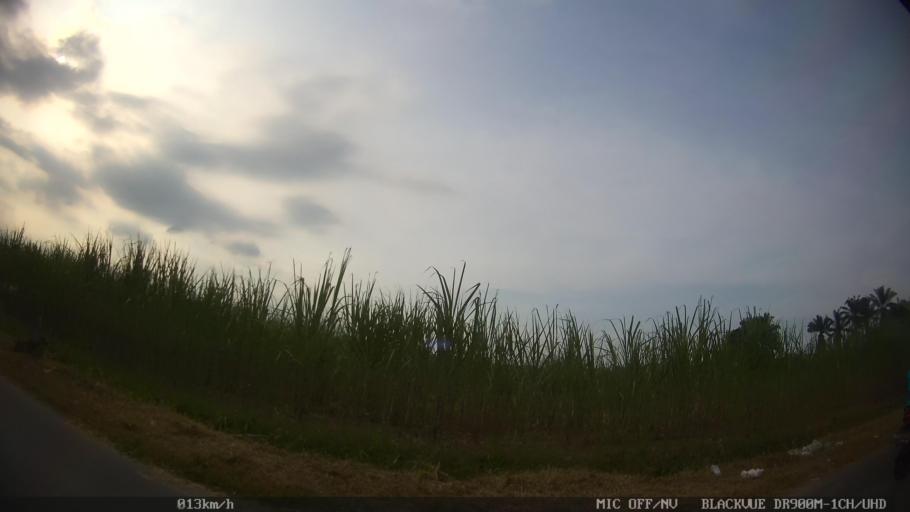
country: ID
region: North Sumatra
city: Binjai
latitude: 3.5925
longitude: 98.5334
